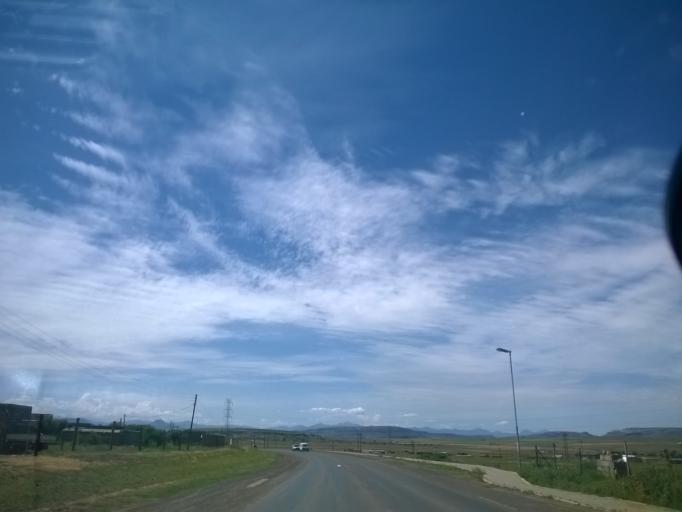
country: LS
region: Leribe
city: Maputsoe
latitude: -28.9148
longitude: 27.9240
